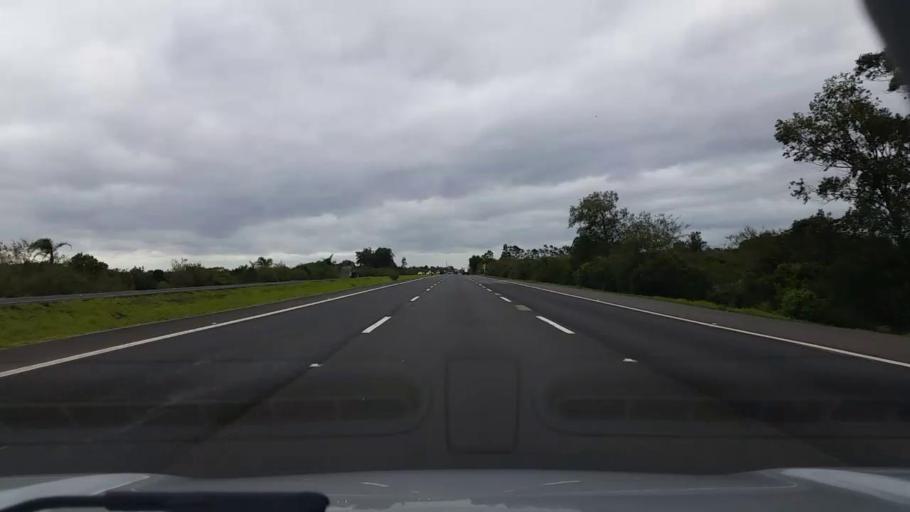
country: BR
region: Rio Grande do Sul
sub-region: Rolante
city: Rolante
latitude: -29.8836
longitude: -50.5517
